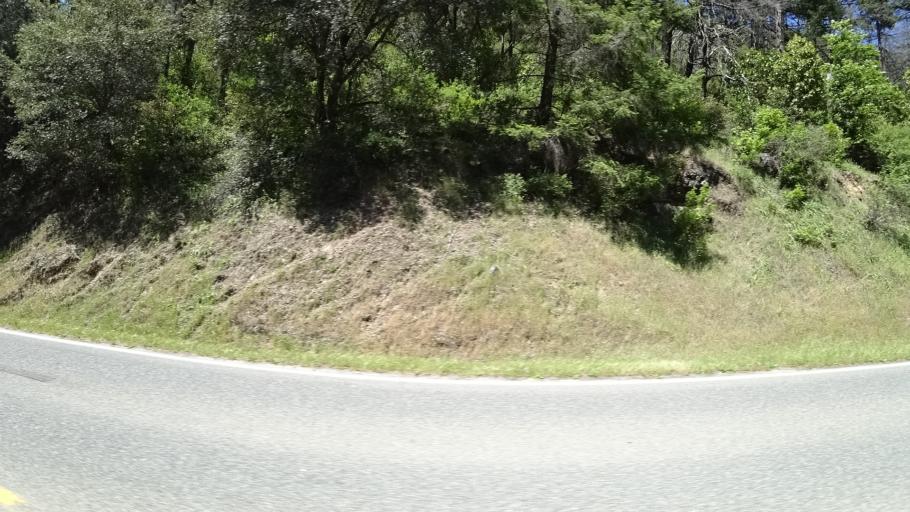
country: US
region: California
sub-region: Trinity County
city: Hayfork
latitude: 40.7754
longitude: -123.3254
